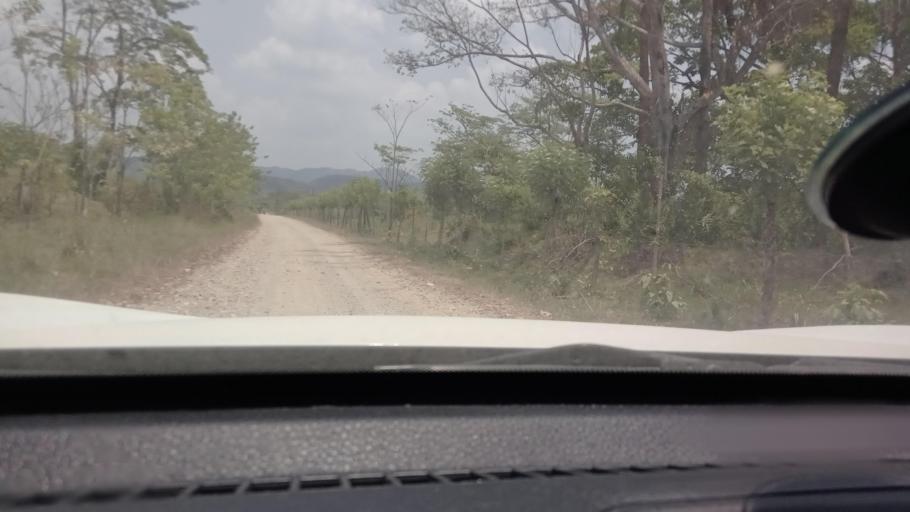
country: MX
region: Tabasco
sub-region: Huimanguillo
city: Francisco Rueda
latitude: 17.5147
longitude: -93.8939
